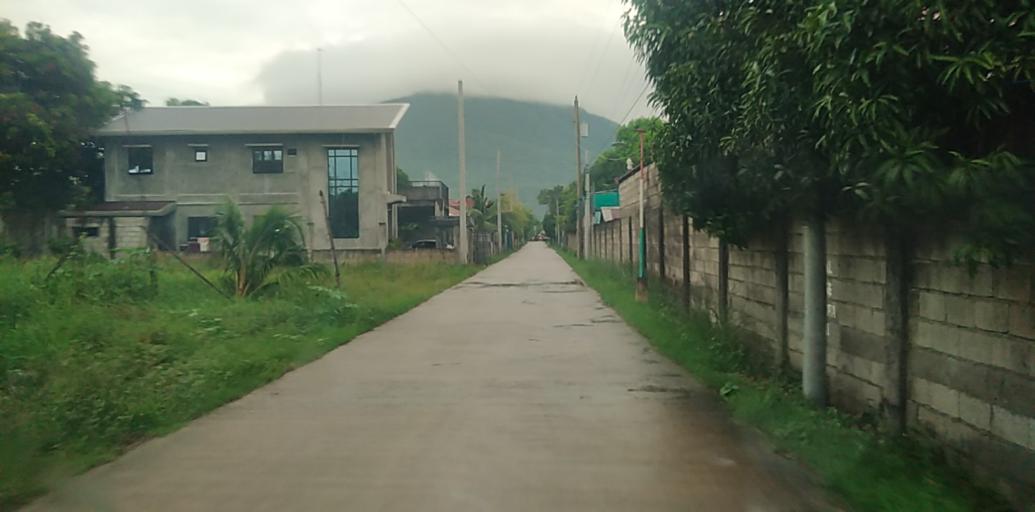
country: PH
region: Central Luzon
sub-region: Province of Pampanga
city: Anao
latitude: 15.1526
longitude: 120.7244
